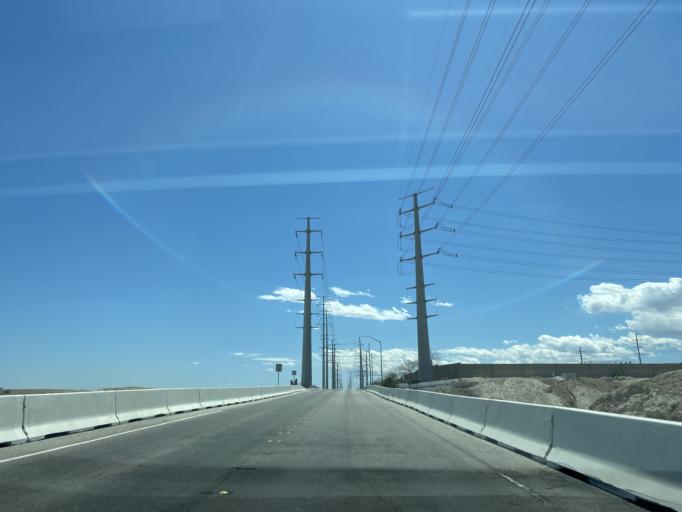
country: US
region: Nevada
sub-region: Clark County
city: North Las Vegas
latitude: 36.3253
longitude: -115.2071
